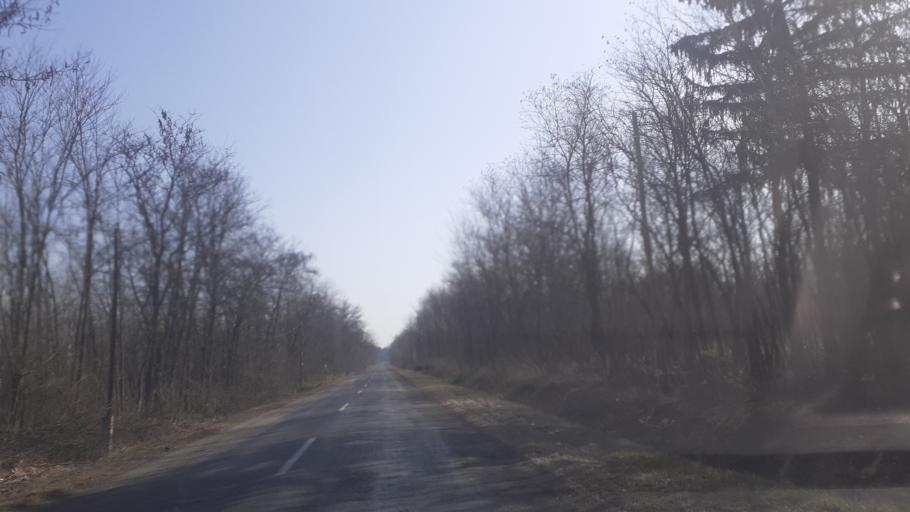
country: HU
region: Pest
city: Orkeny
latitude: 47.0646
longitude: 19.3966
